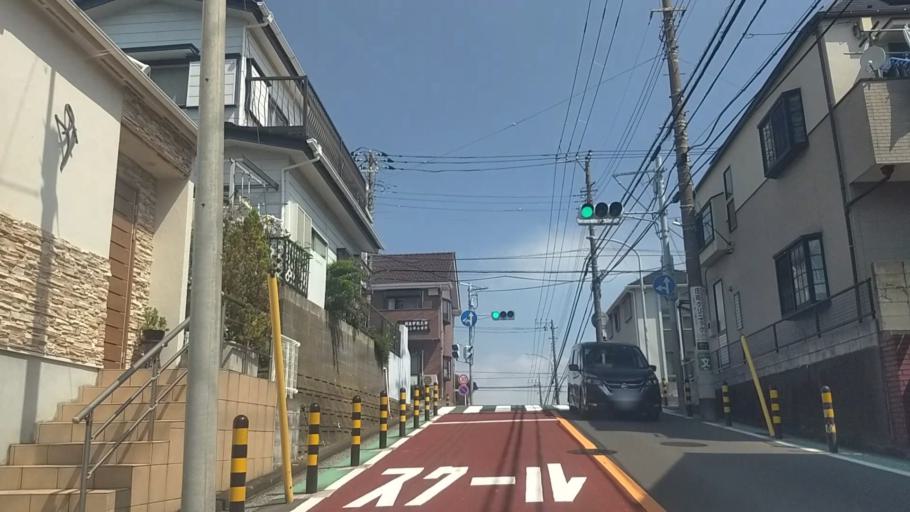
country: JP
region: Kanagawa
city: Zushi
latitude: 35.3326
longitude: 139.6038
